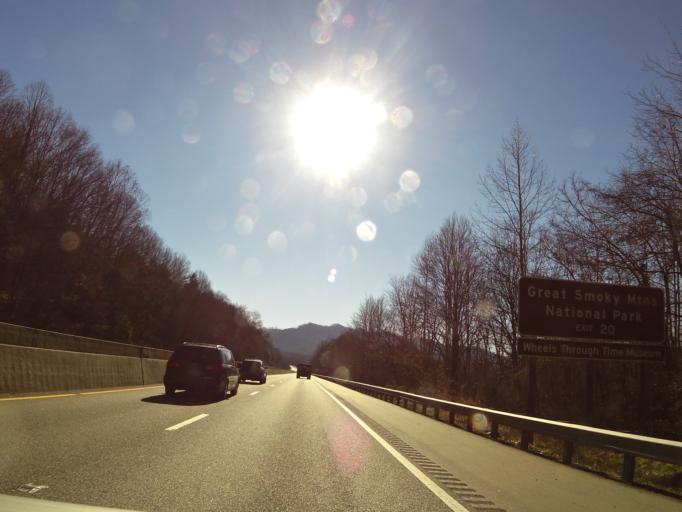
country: US
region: North Carolina
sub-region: Haywood County
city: Cove Creek
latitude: 35.6111
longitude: -83.0113
